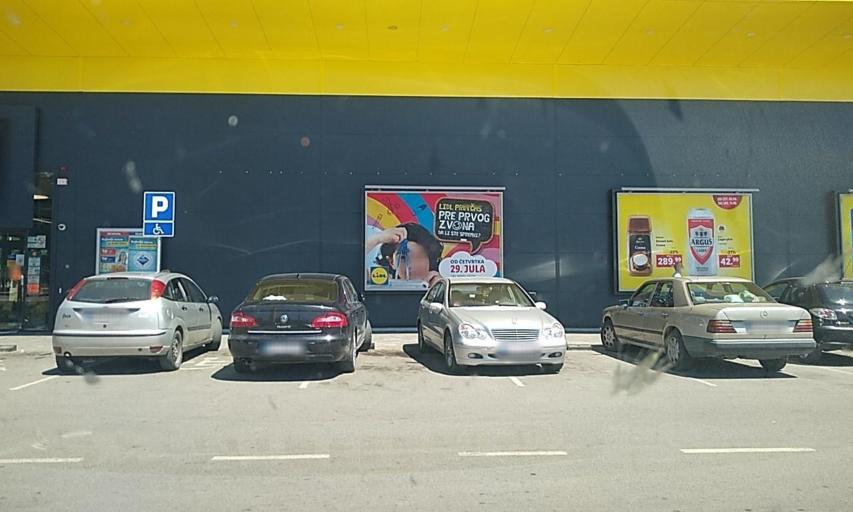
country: RS
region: Central Serbia
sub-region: Branicevski Okrug
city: Pozarevac
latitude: 44.6107
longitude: 21.1746
